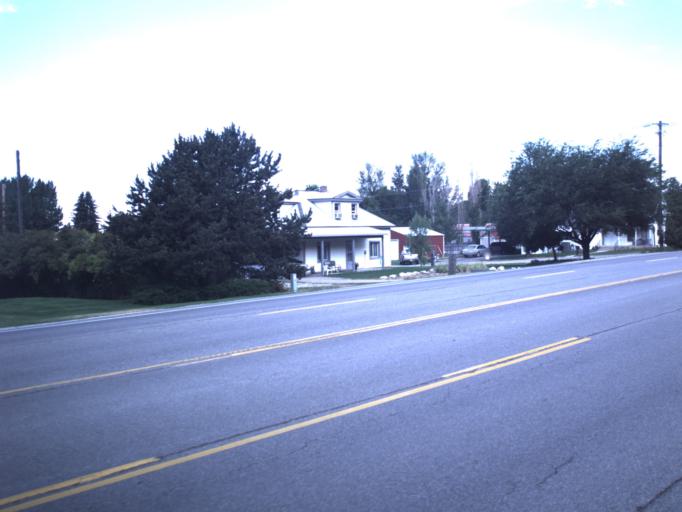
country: US
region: Utah
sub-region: Box Elder County
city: Willard
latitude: 41.4099
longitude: -112.0362
